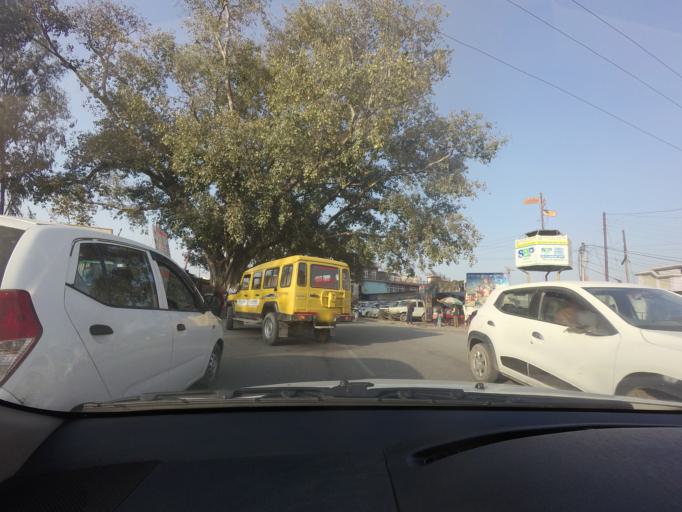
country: IN
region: Himachal Pradesh
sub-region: Mandi
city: Sundarnagar
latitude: 31.5512
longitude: 76.8994
